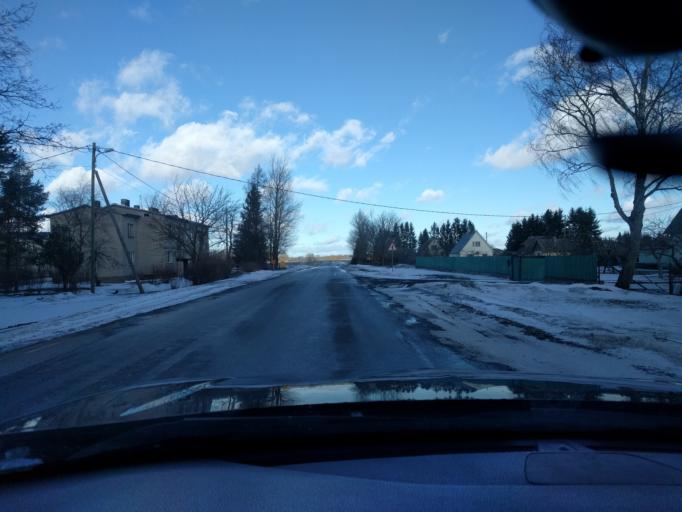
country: EE
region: Harju
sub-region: Raasiku vald
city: Raasiku
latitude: 59.3378
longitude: 25.1531
